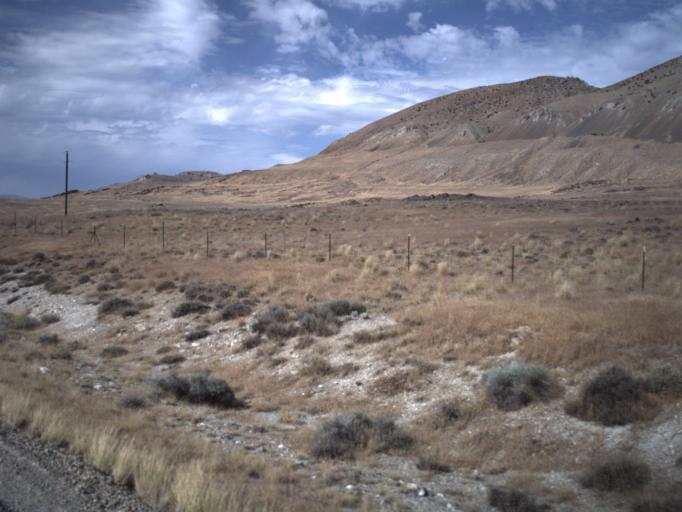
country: US
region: Utah
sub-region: Tooele County
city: Wendover
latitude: 41.4731
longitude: -113.6381
